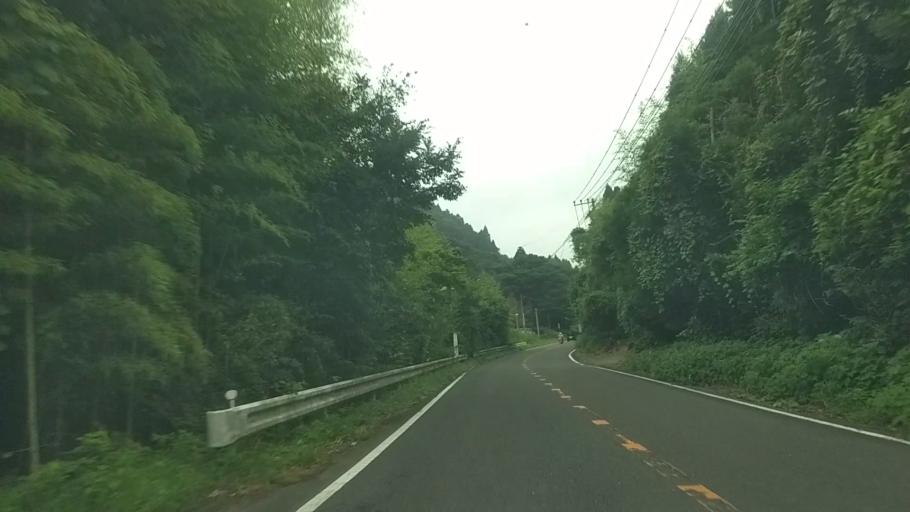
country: JP
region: Chiba
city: Kawaguchi
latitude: 35.1412
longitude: 139.9486
